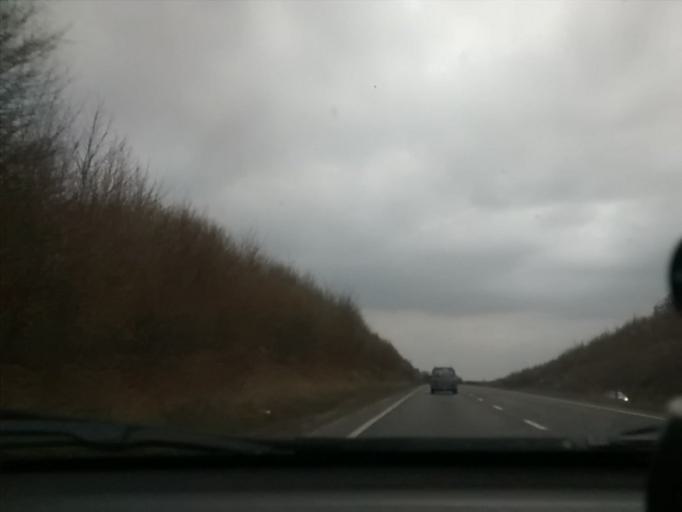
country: GB
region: England
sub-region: Cambridgeshire
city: Sawston
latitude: 52.0969
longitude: 0.2058
